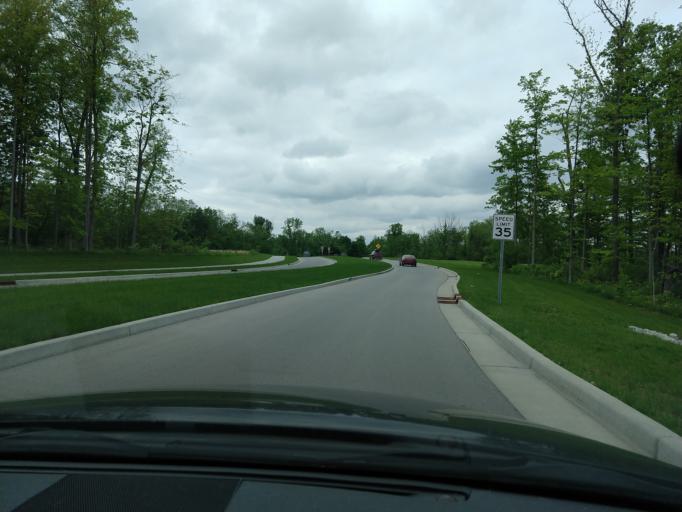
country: US
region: Indiana
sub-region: Hamilton County
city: Carmel
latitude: 40.0094
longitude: -86.1306
